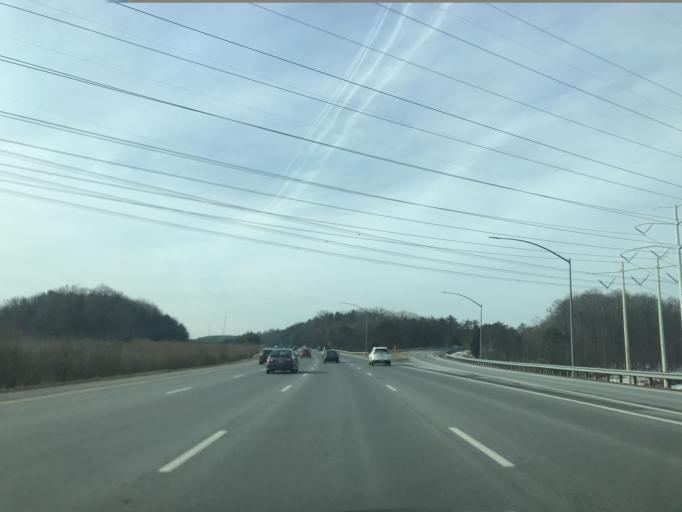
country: US
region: Maryland
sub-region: Howard County
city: North Laurel
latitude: 39.1339
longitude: -76.8566
